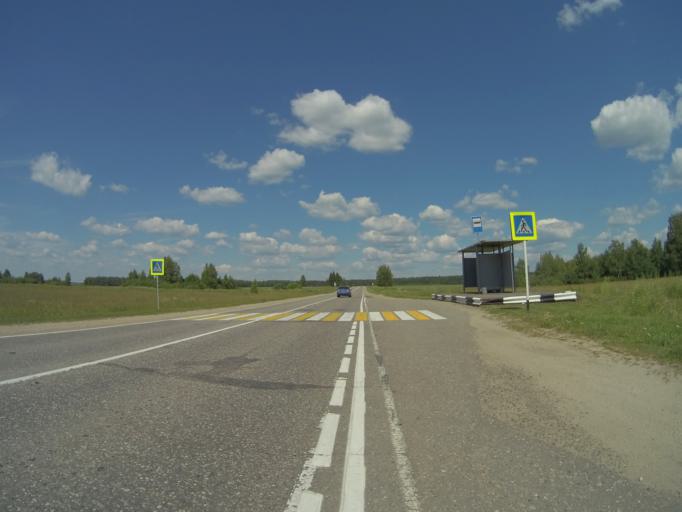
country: RU
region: Ivanovo
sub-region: Privolzhskiy Rayon
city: Ples
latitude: 57.4042
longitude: 41.4195
